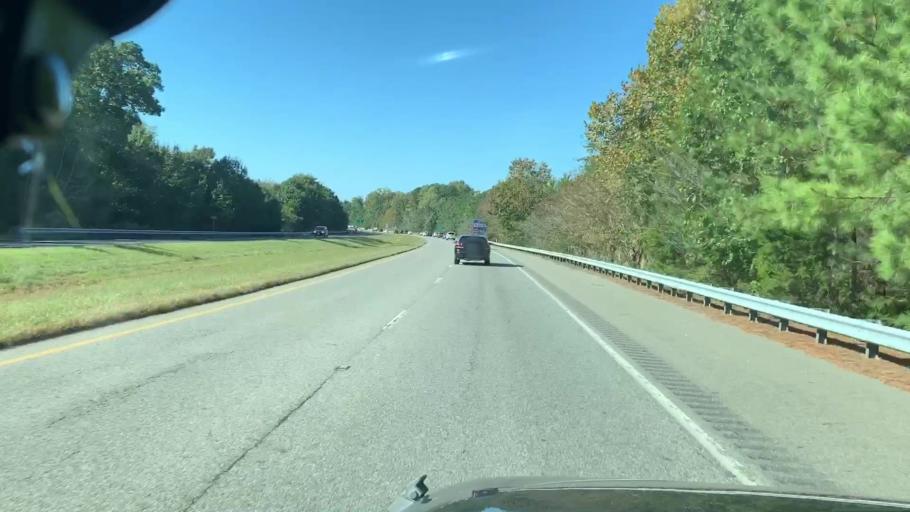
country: US
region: Virginia
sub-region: James City County
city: Williamsburg
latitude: 37.2654
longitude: -76.7427
